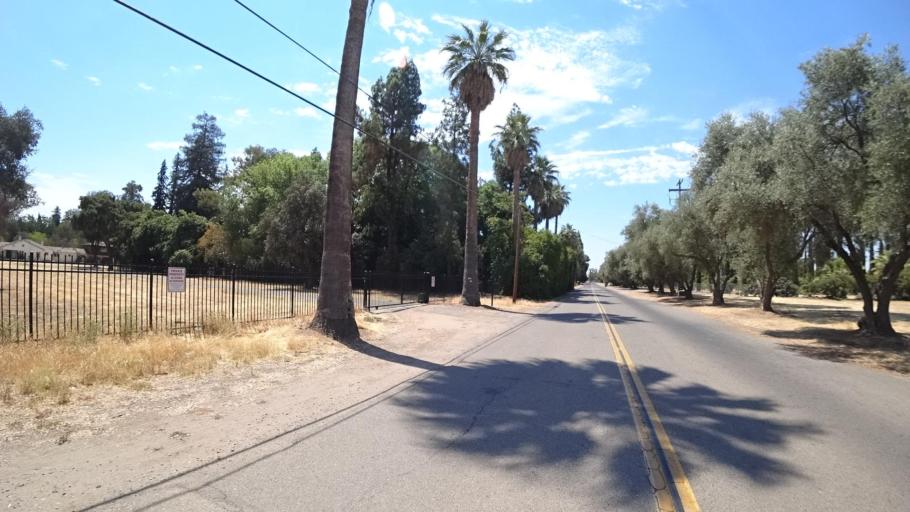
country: US
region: California
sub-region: Fresno County
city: Sunnyside
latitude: 36.7257
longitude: -119.7094
